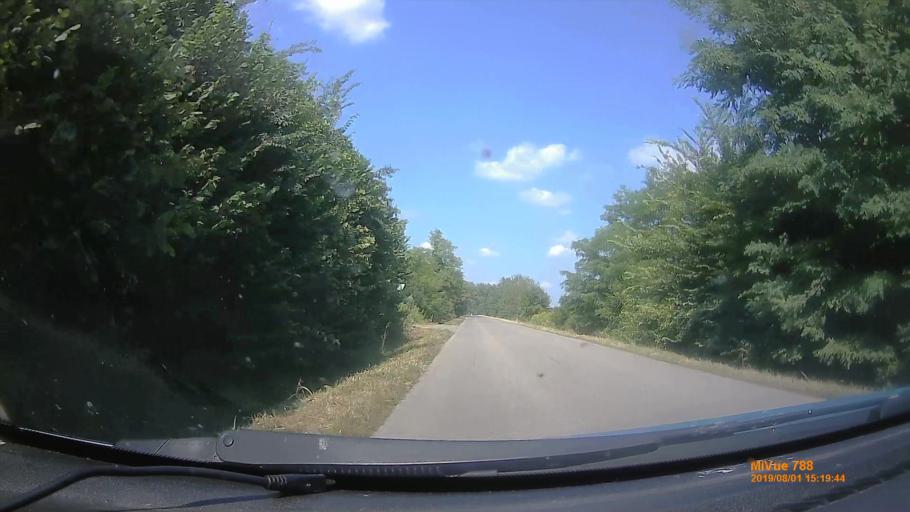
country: HU
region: Baranya
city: Sellye
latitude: 45.8570
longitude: 17.8268
